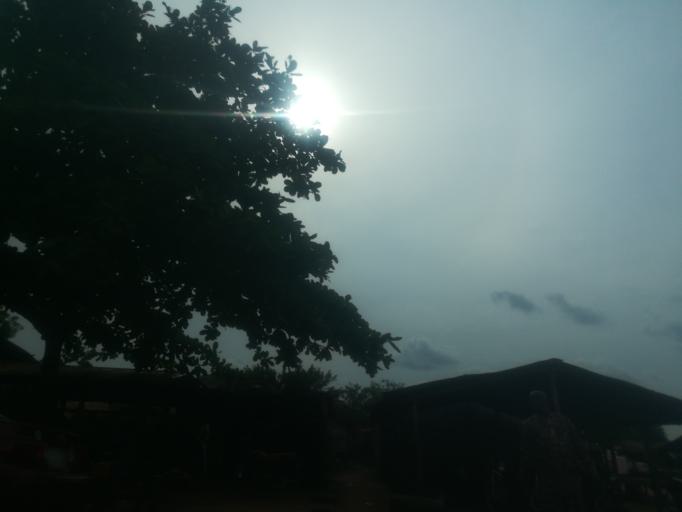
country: NG
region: Ogun
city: Ayetoro
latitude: 7.3130
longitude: 3.0712
